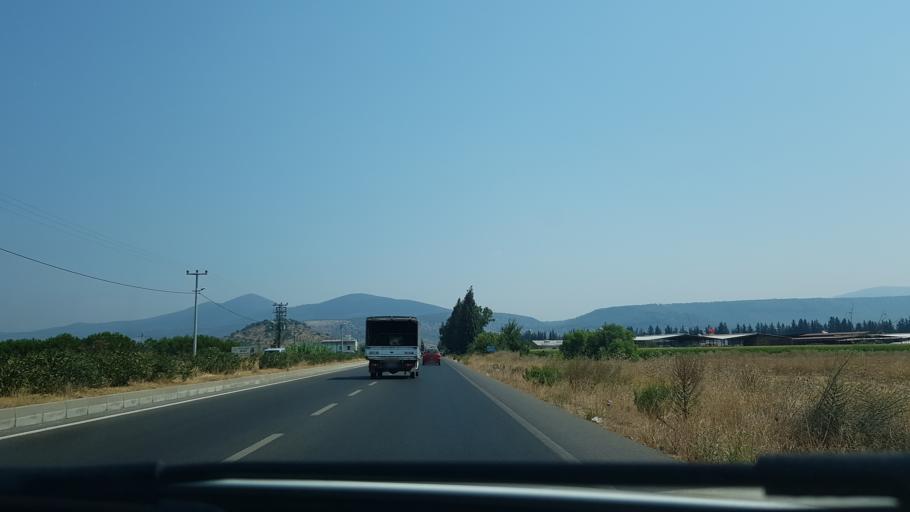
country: TR
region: Mugla
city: Milas
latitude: 37.2461
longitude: 27.7204
